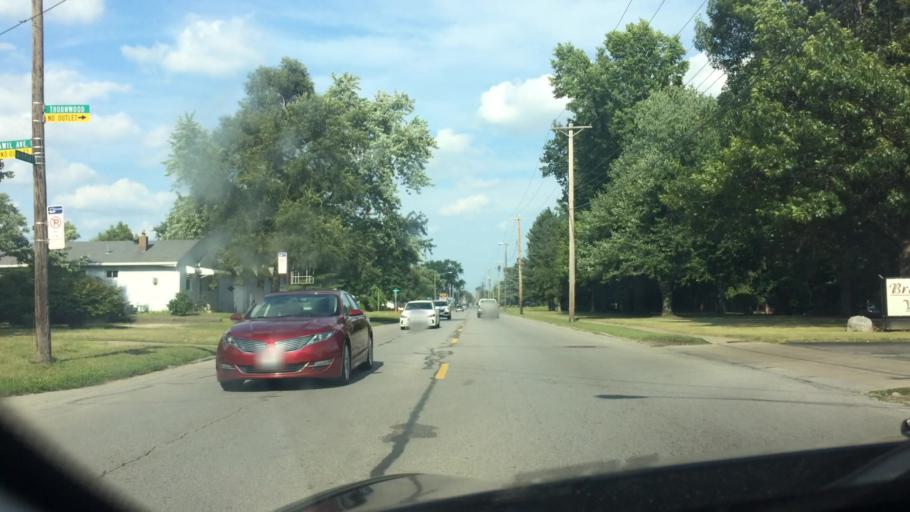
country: US
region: Ohio
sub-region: Lucas County
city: Ottawa Hills
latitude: 41.6254
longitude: -83.6209
